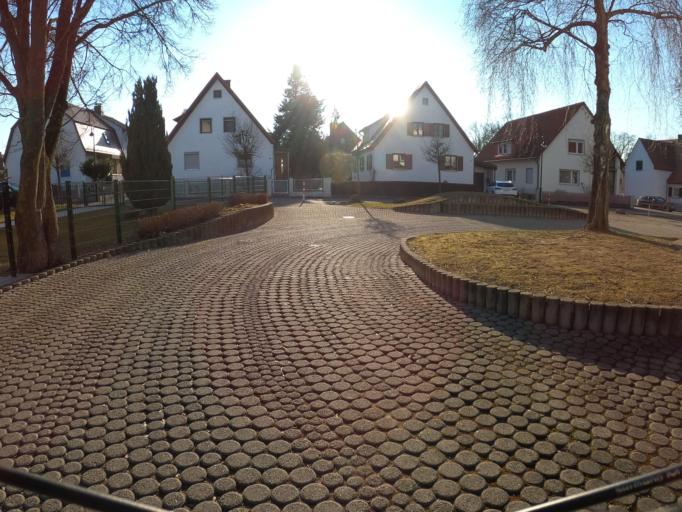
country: DE
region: Bavaria
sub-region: Swabia
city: Leipheim
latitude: 48.4516
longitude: 10.2225
